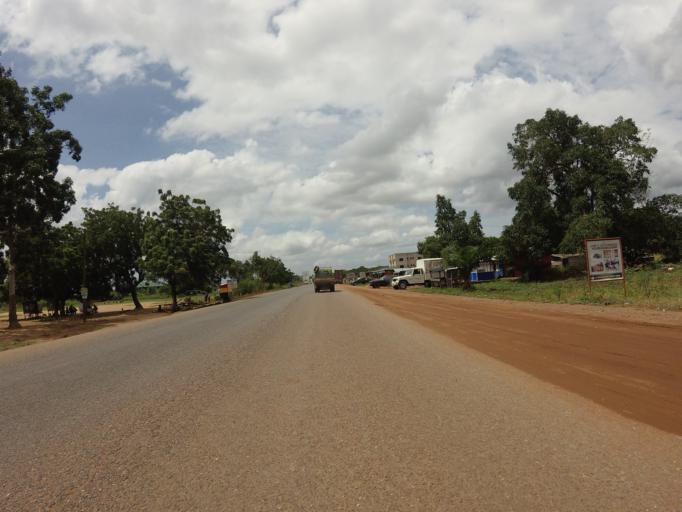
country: GH
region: Eastern
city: Aburi
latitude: 5.8363
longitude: -0.1168
